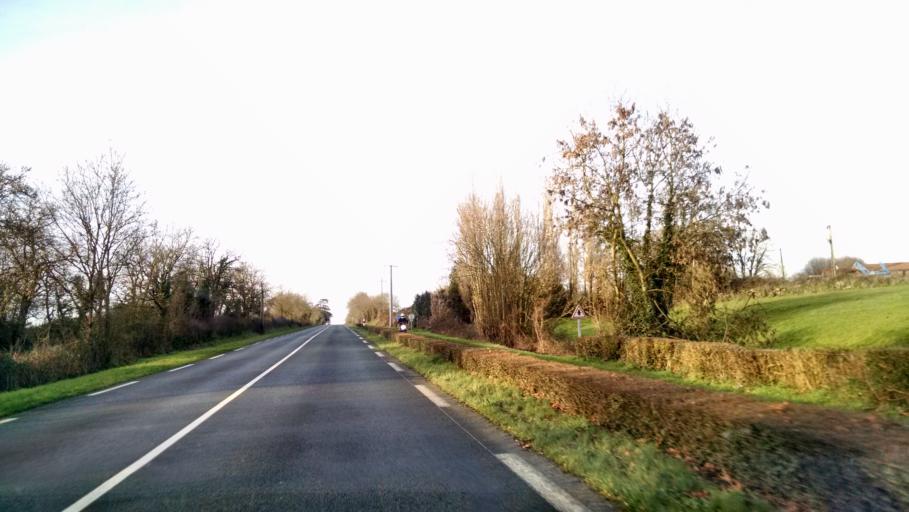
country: FR
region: Pays de la Loire
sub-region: Departement de la Vendee
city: Montaigu
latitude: 46.9858
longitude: -1.3202
